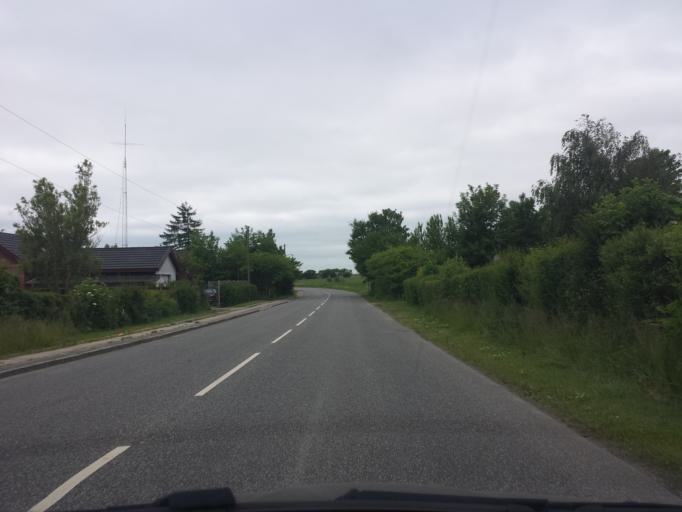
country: DK
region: Capital Region
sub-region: Ballerup Kommune
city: Ballerup
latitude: 55.7087
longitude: 12.3780
